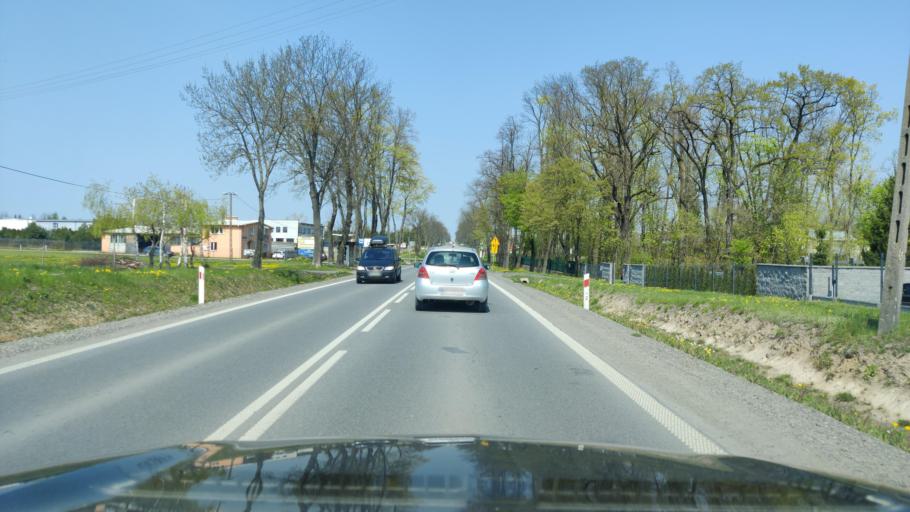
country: PL
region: Masovian Voivodeship
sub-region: Powiat pultuski
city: Pultusk
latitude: 52.6697
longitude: 21.0814
